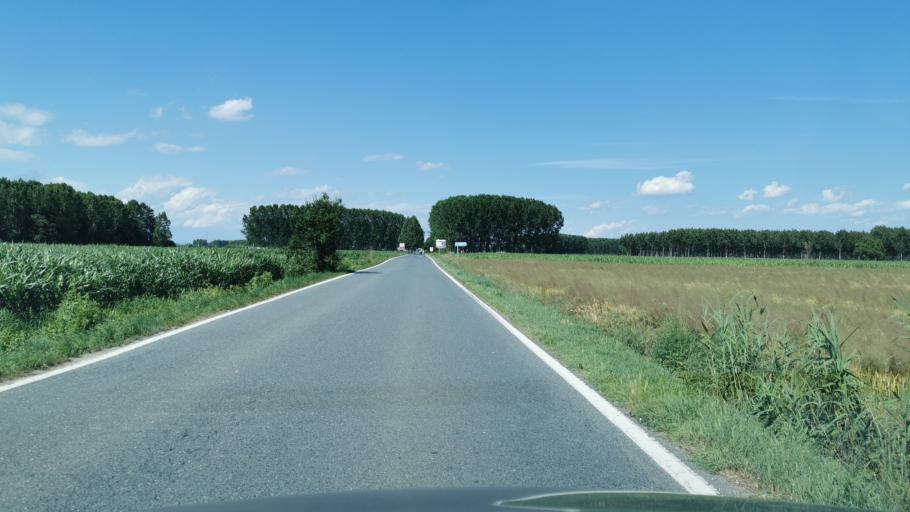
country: IT
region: Piedmont
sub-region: Provincia di Torino
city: Airasca
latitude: 44.9250
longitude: 7.4959
